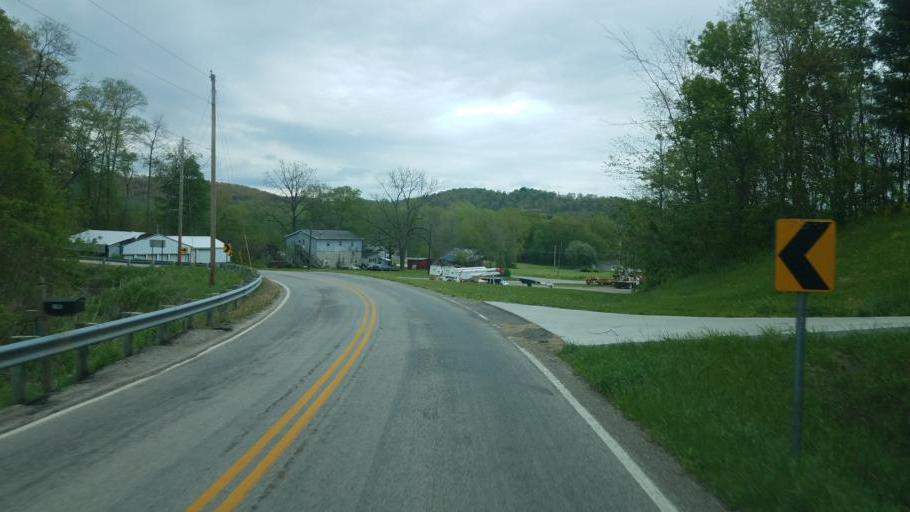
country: US
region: Ohio
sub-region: Ashland County
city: Loudonville
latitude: 40.6552
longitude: -82.3201
